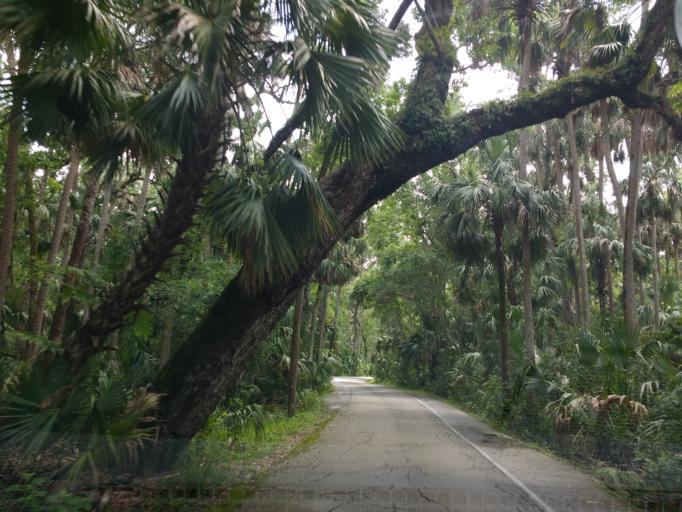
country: US
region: Florida
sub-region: Highlands County
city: Sebring
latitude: 27.4706
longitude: -81.5470
